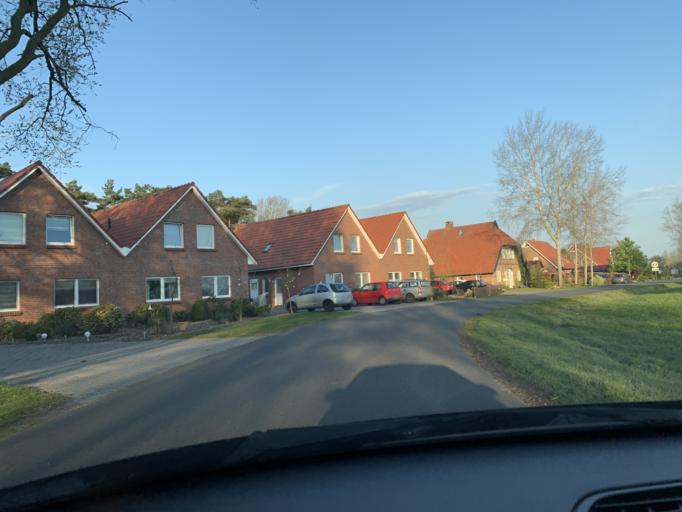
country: DE
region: Lower Saxony
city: Apen
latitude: 53.2910
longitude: 7.8296
